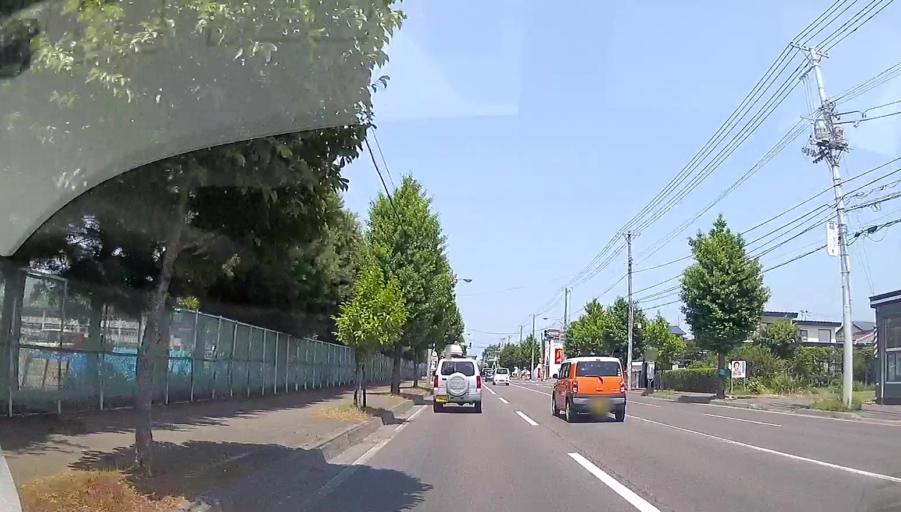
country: JP
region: Hokkaido
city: Obihiro
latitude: 42.9016
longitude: 143.2000
